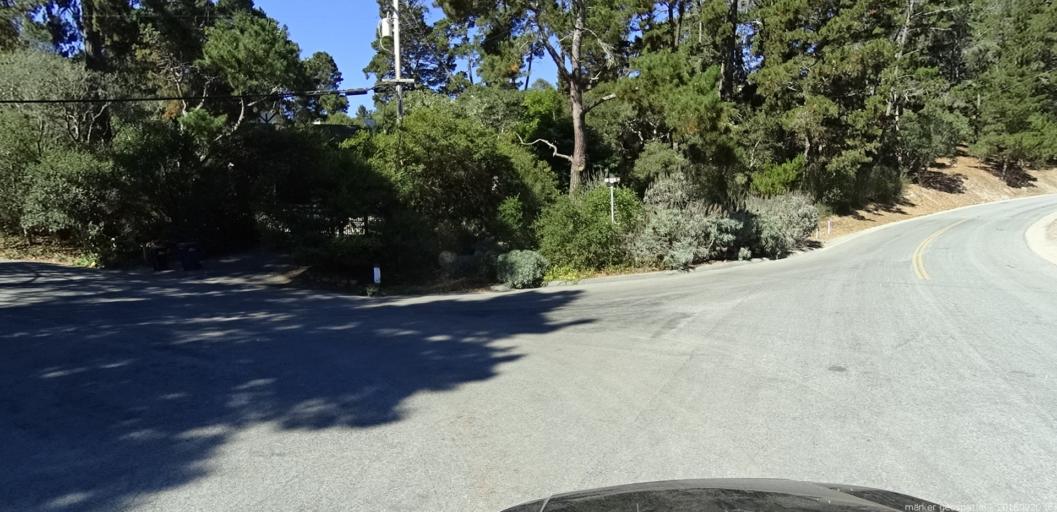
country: US
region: California
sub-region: Monterey County
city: Carmel-by-the-Sea
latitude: 36.5551
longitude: -121.8974
